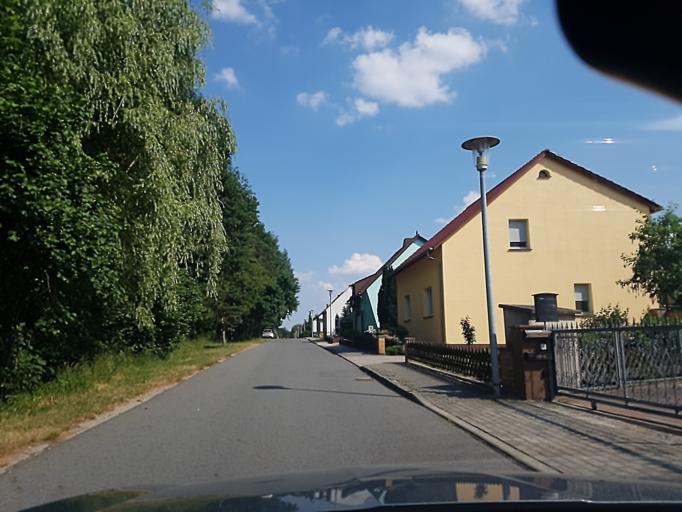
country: DE
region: Brandenburg
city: Ruckersdorf
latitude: 51.5630
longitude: 13.5545
